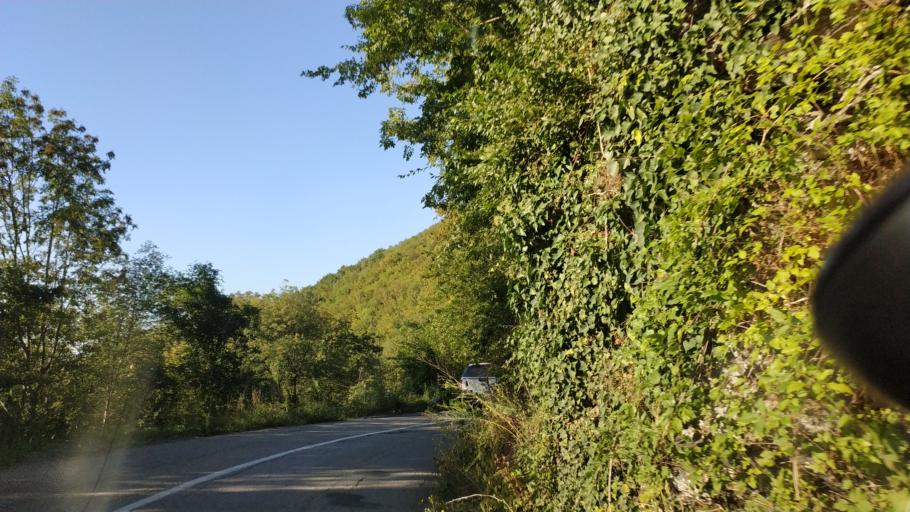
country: RS
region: Central Serbia
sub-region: Rasinski Okrug
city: Krusevac
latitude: 43.4639
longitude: 21.3598
